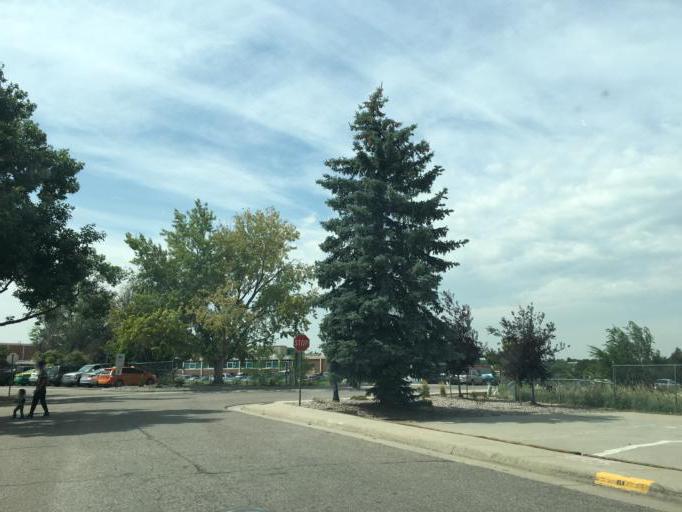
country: US
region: Colorado
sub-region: Adams County
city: Aurora
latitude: 39.7360
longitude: -104.8073
